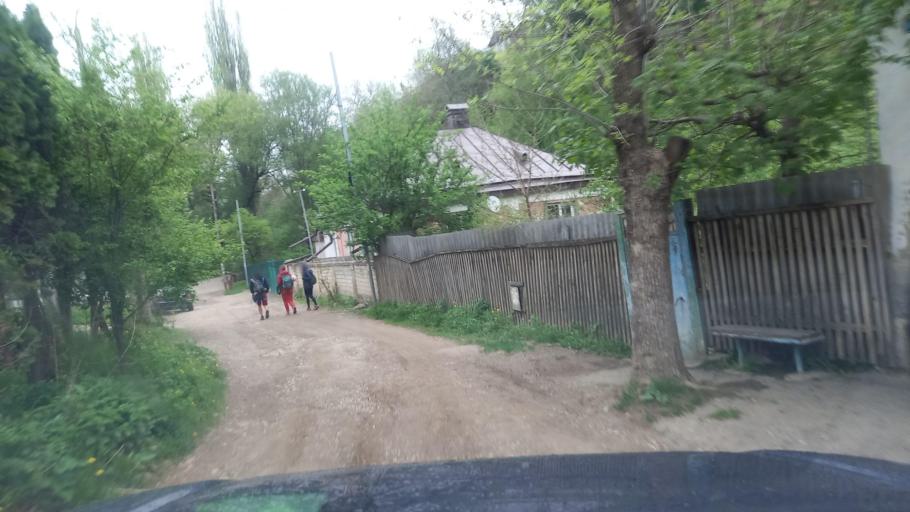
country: RU
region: Stavropol'skiy
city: Kislovodsk
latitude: 43.8911
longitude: 42.7099
